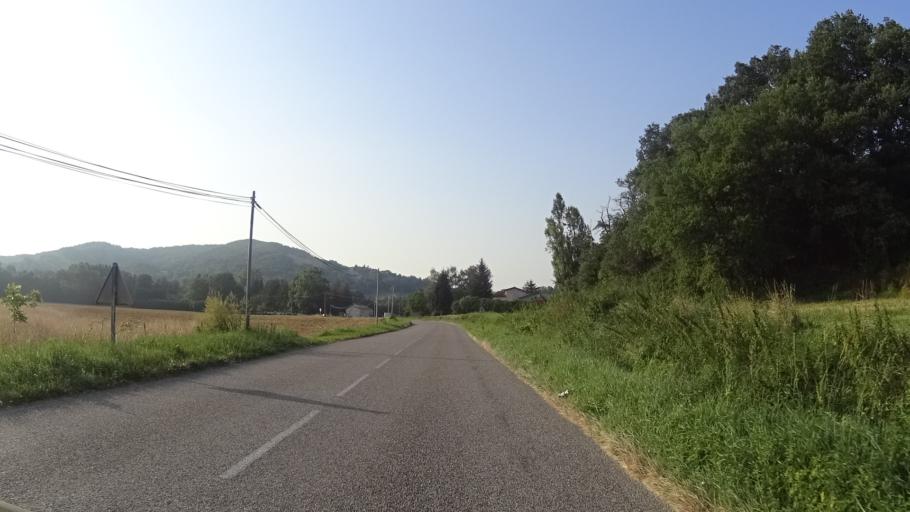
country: FR
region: Midi-Pyrenees
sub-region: Departement de l'Ariege
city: Mirepoix
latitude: 43.0761
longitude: 1.9388
